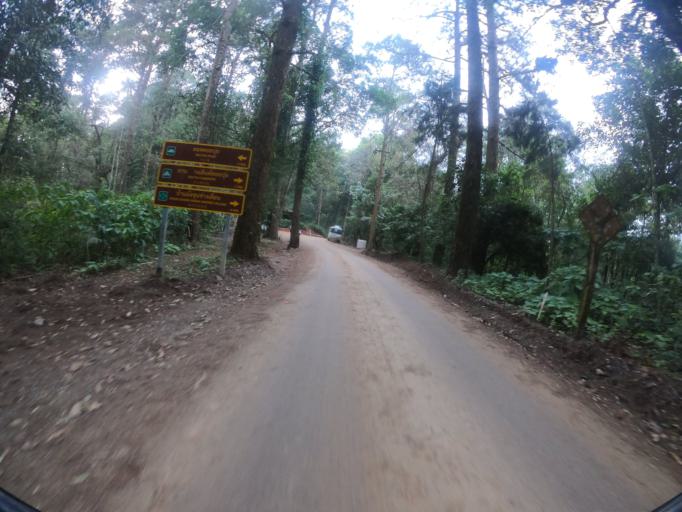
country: TH
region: Chiang Mai
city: Chiang Mai
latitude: 18.8227
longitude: 98.8902
